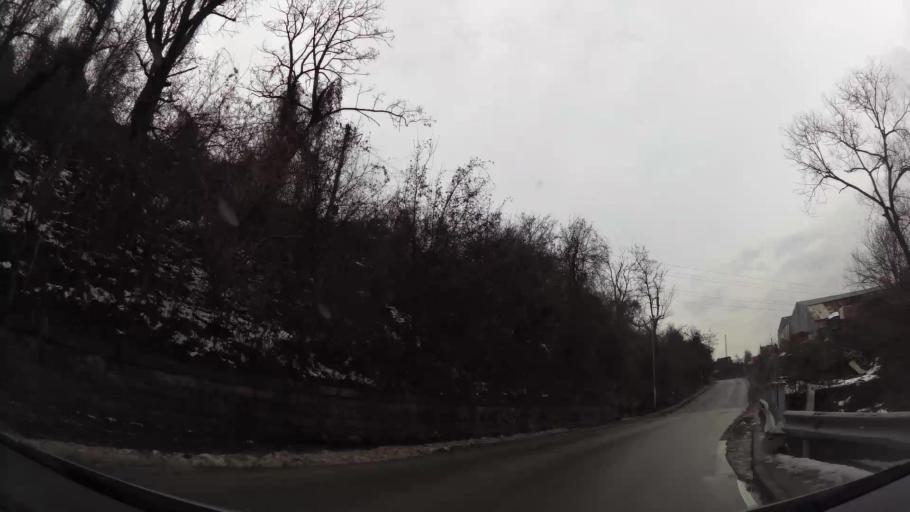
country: BG
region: Sofia-Capital
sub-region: Stolichna Obshtina
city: Sofia
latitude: 42.6703
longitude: 23.2415
